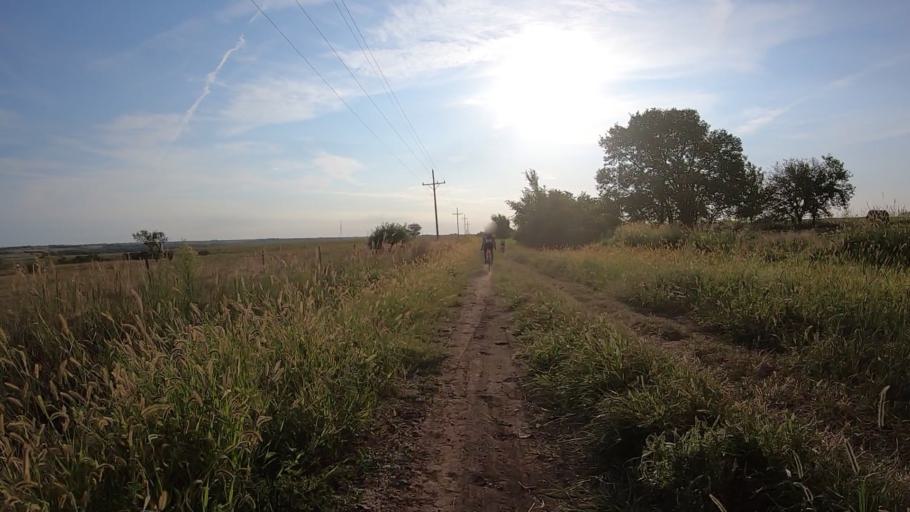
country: US
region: Kansas
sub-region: Marshall County
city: Blue Rapids
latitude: 39.7115
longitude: -96.7987
